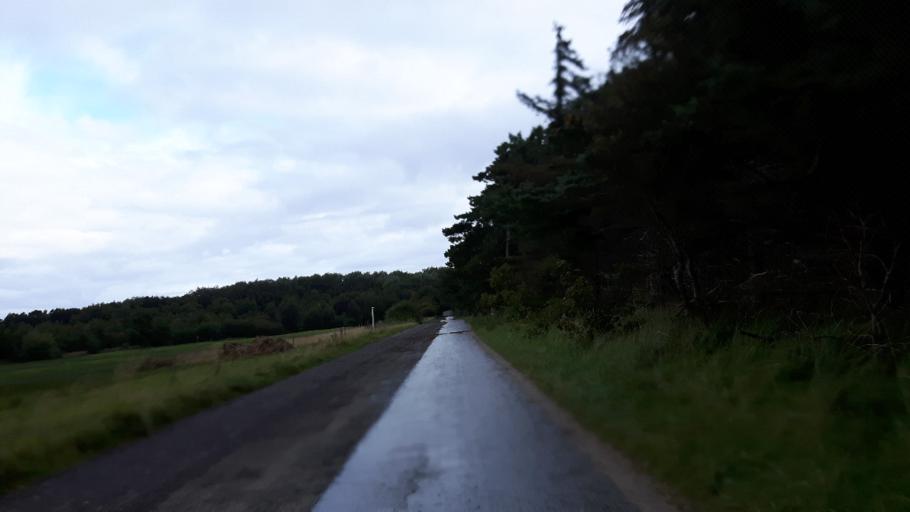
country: NL
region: Friesland
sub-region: Gemeente Ameland
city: Nes
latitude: 53.4506
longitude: 5.7572
